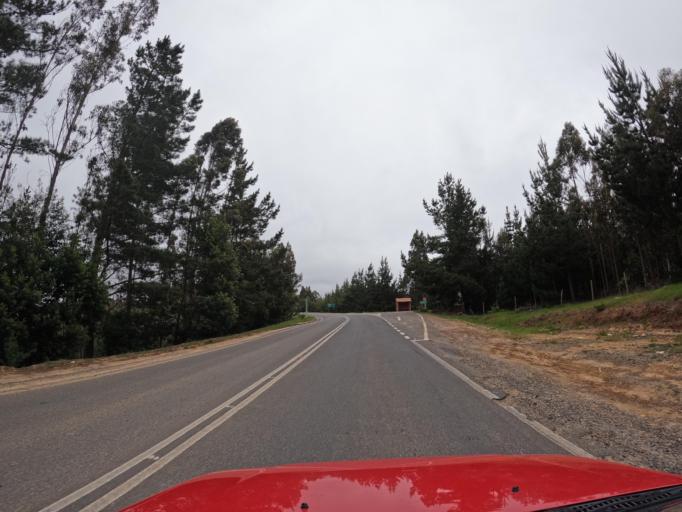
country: CL
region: O'Higgins
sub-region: Provincia de Colchagua
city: Santa Cruz
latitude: -34.6110
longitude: -72.0135
